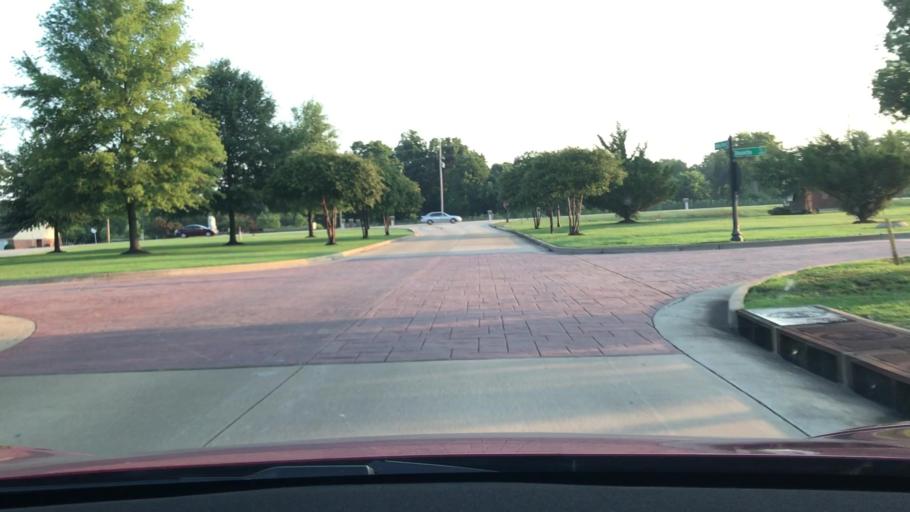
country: US
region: Louisiana
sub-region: Bossier Parish
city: Bossier City
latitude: 32.3999
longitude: -93.7105
